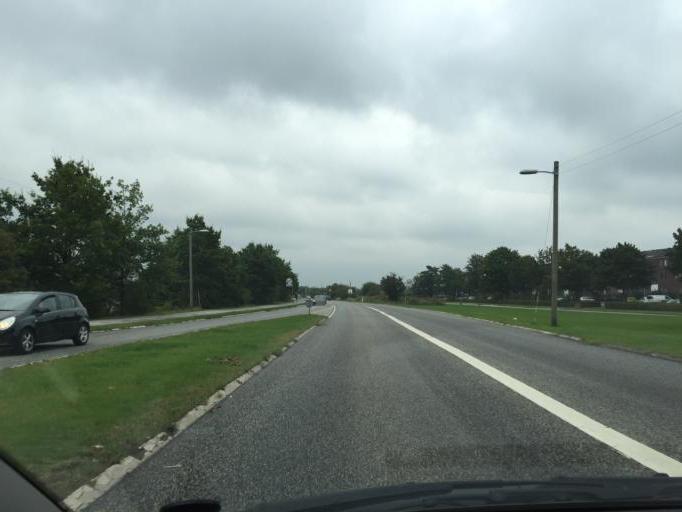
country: DK
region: Capital Region
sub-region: Herlev Kommune
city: Herlev
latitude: 55.7448
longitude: 12.4347
